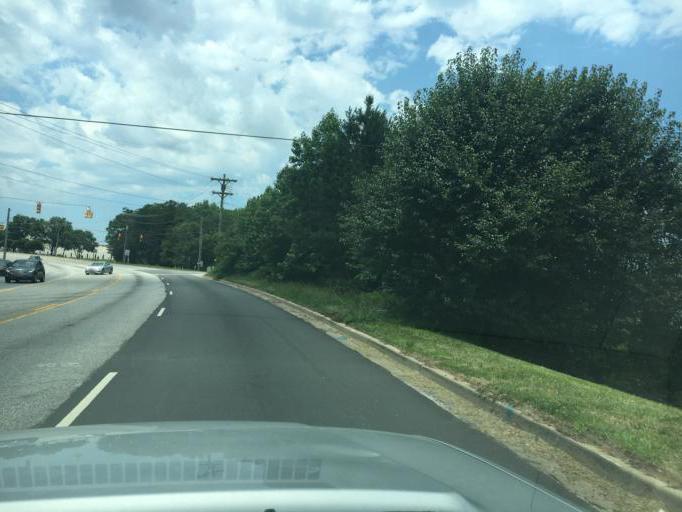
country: US
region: South Carolina
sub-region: Greenville County
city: Five Forks
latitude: 34.8524
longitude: -82.2316
